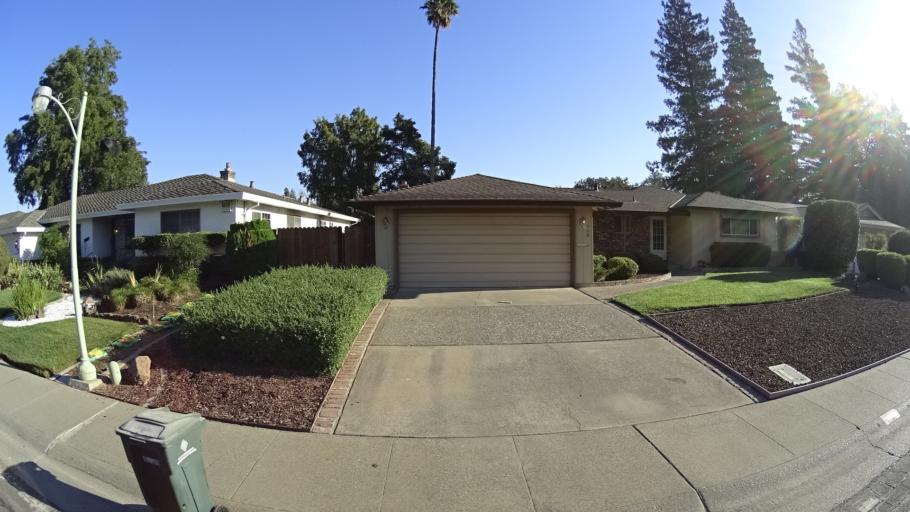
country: US
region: California
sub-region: Yolo County
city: West Sacramento
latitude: 38.5074
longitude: -121.5505
